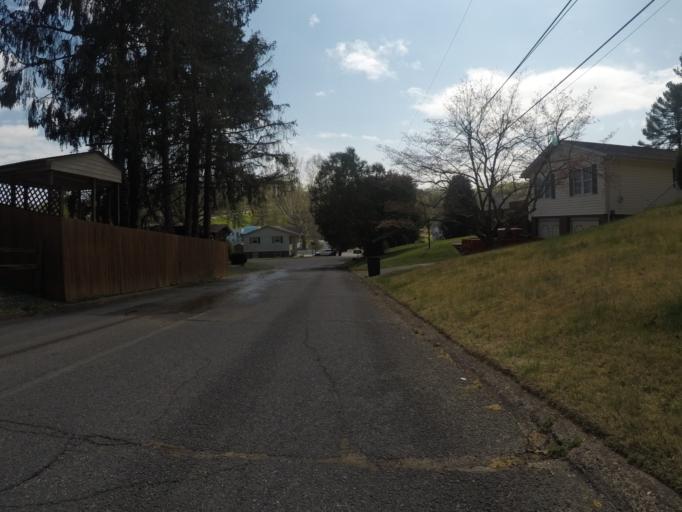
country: US
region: Ohio
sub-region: Lawrence County
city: Burlington
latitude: 38.3852
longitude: -82.5195
